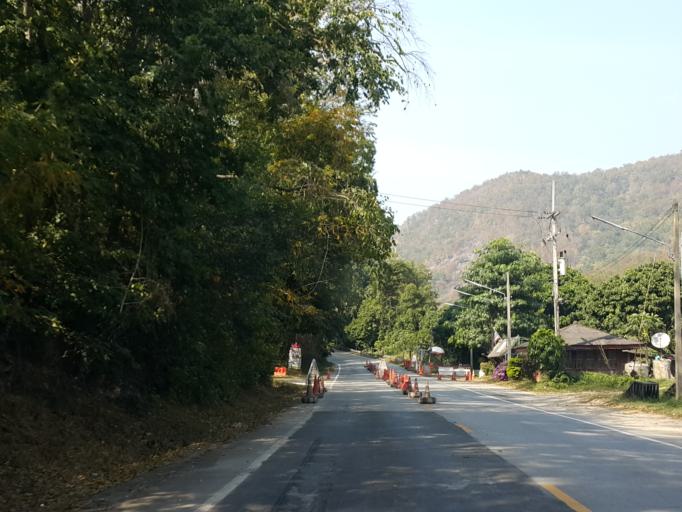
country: TH
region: Chiang Mai
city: Hot
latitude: 18.2214
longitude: 98.4761
